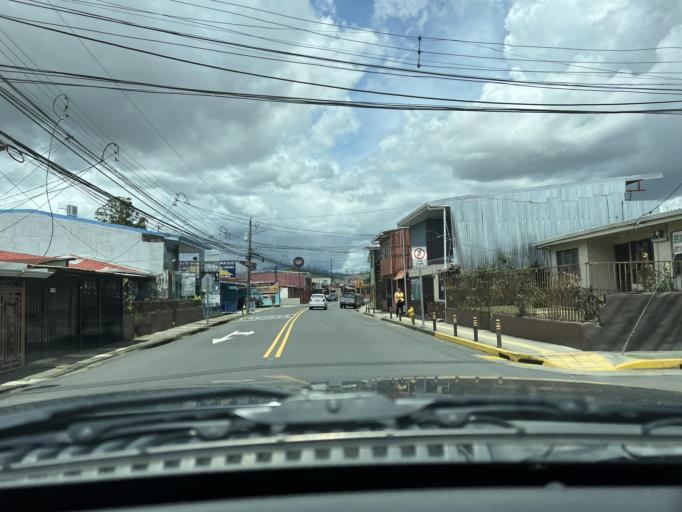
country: CR
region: San Jose
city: Sabanilla
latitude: 9.9416
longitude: -84.0276
